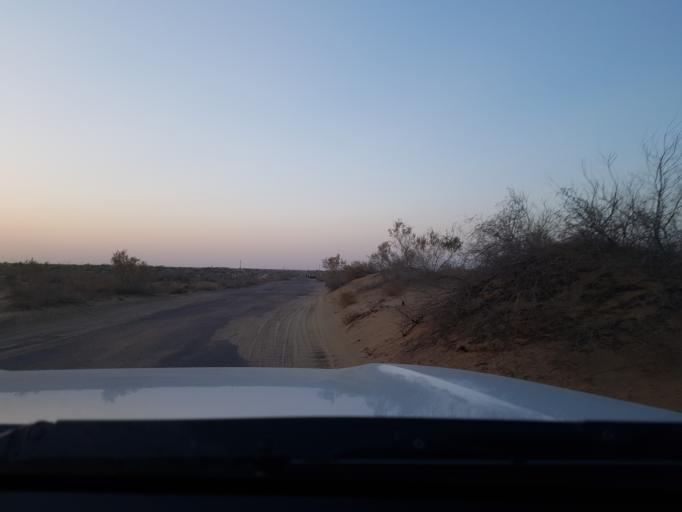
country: UZ
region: Xorazm
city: Khiwa
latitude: 41.2815
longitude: 60.3066
